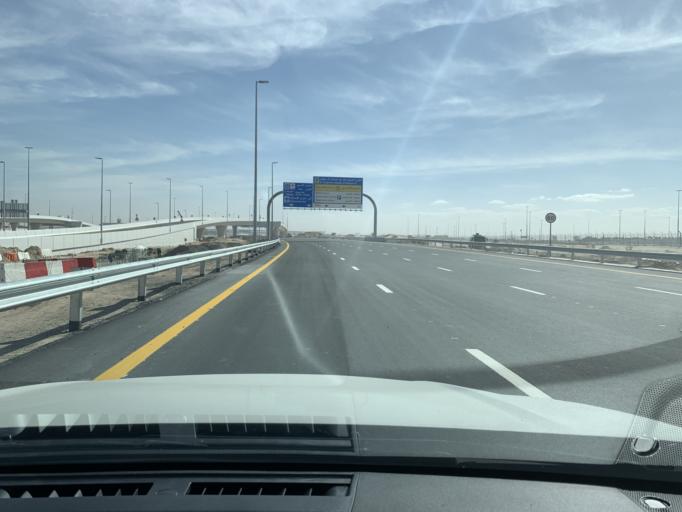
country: AE
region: Dubai
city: Dubai
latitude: 24.9676
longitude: 55.1645
